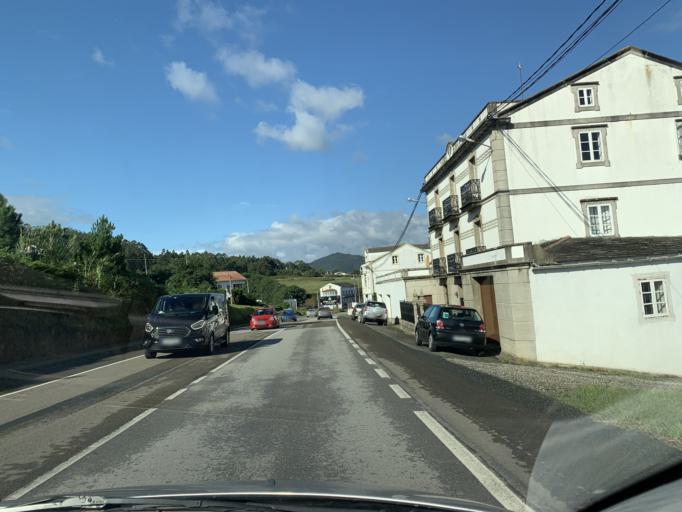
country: ES
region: Galicia
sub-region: Provincia de Lugo
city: Barreiros
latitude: 43.5401
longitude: -7.2354
